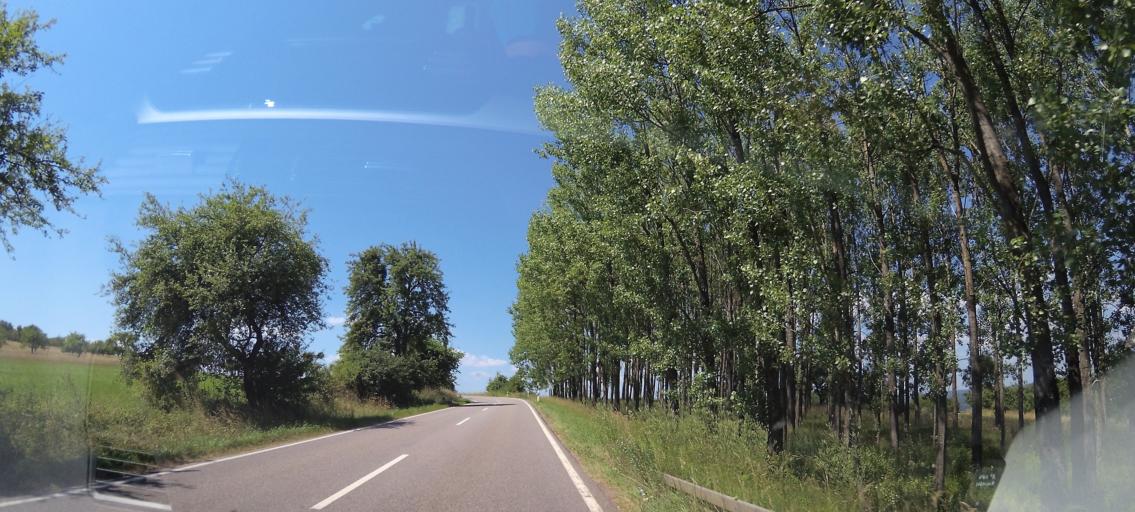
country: DE
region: Saarland
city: Merzig
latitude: 49.4354
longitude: 6.6005
